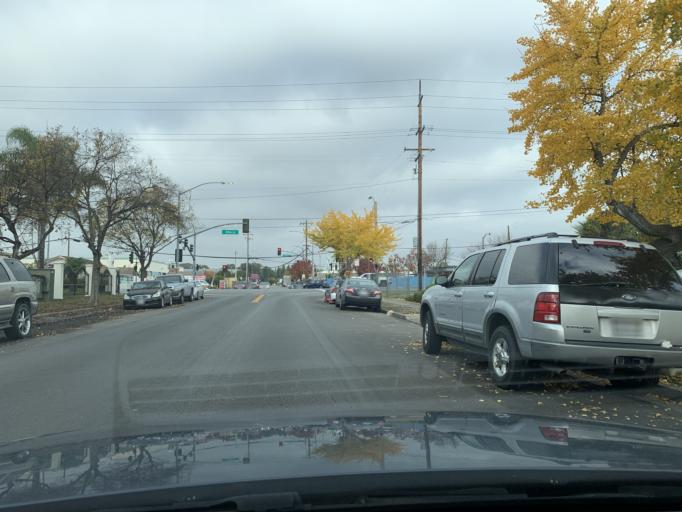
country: US
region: California
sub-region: Santa Clara County
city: Alum Rock
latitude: 37.3337
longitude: -121.8510
